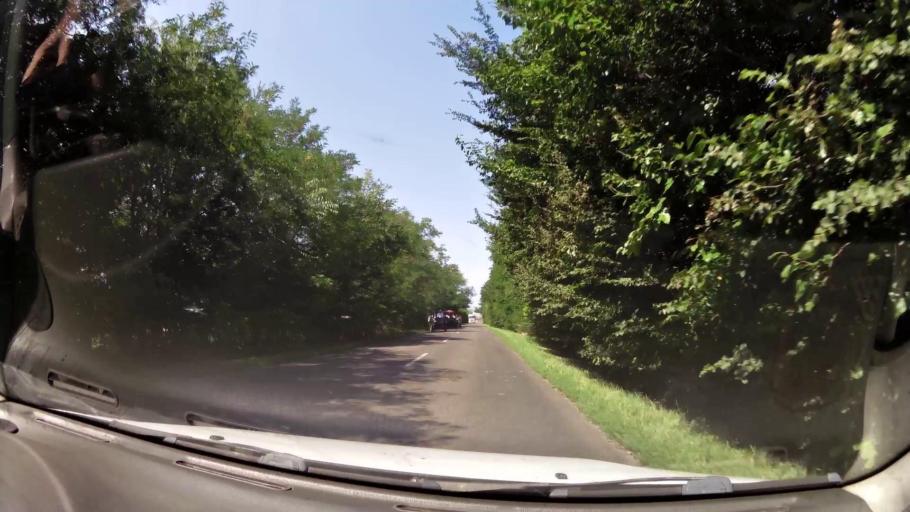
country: HU
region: Pest
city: Tapiosag
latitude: 47.3941
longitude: 19.6380
